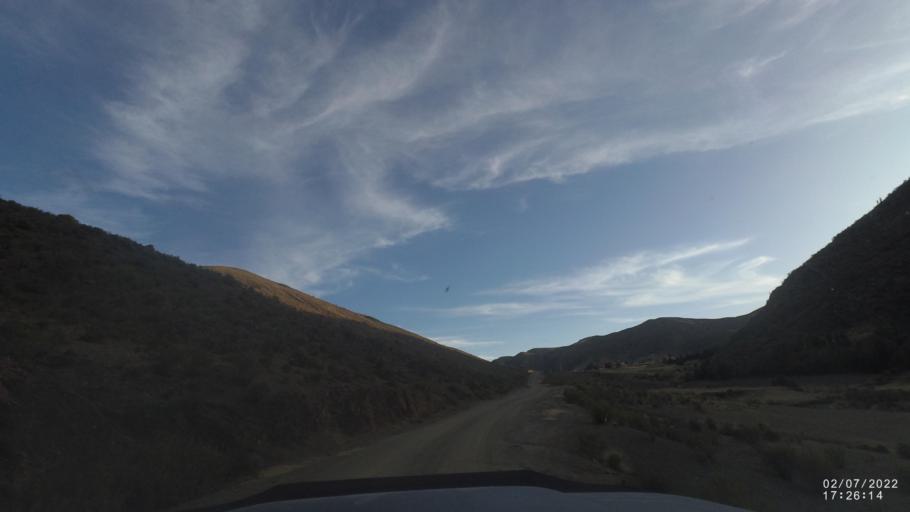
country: BO
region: Cochabamba
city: Irpa Irpa
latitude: -17.8794
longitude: -66.6098
